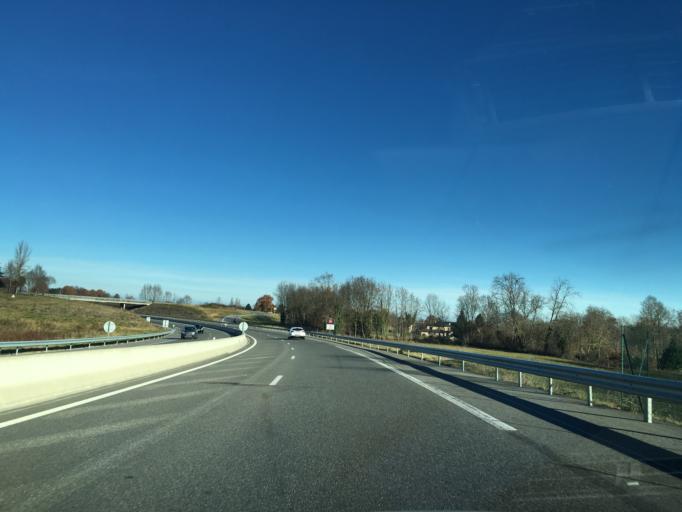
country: FR
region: Midi-Pyrenees
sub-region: Departement des Hautes-Pyrenees
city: Juillan
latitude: 43.1809
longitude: 0.0127
